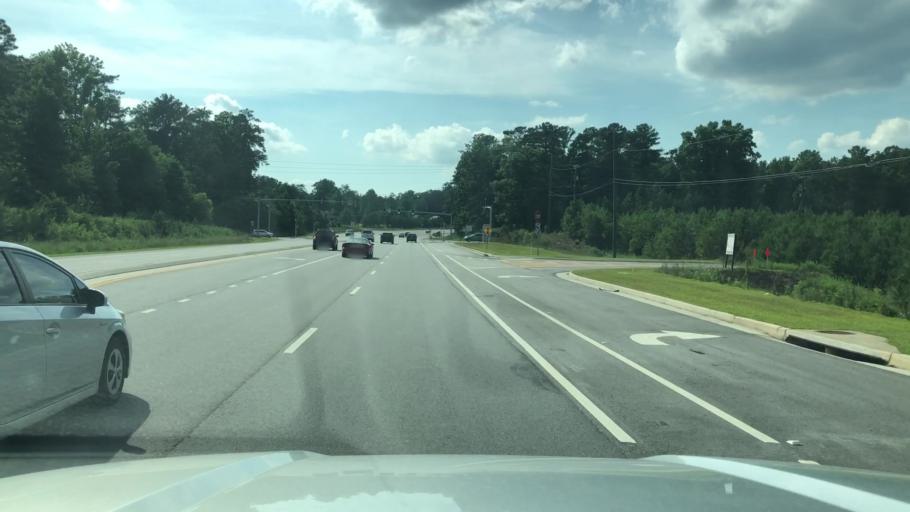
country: US
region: Georgia
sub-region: Paulding County
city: Hiram
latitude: 33.8603
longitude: -84.7768
